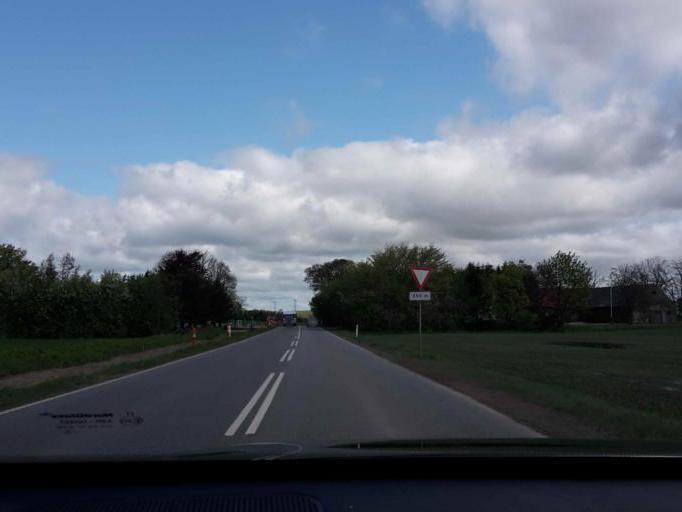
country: DK
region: Central Jutland
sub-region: Syddjurs Kommune
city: Hornslet
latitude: 56.3025
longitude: 10.3169
